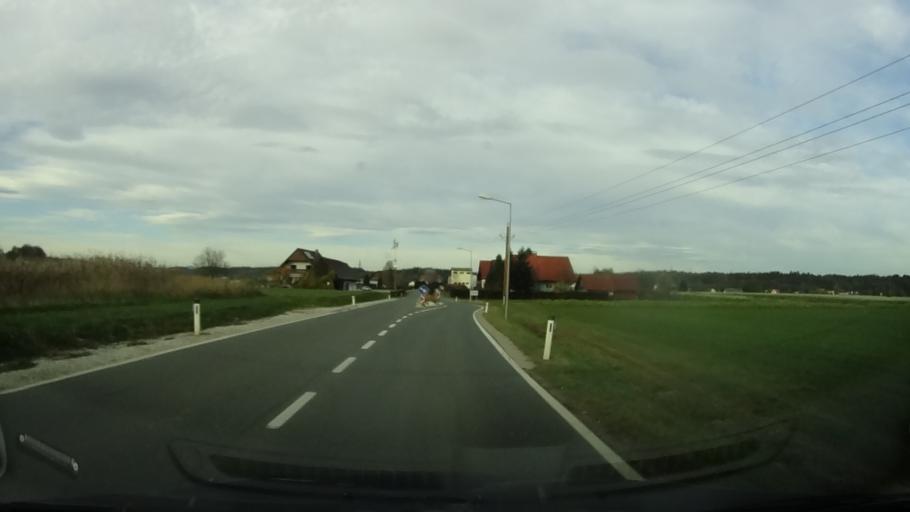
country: AT
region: Styria
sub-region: Politischer Bezirk Leibnitz
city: Hengsberg
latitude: 46.9042
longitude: 15.4080
